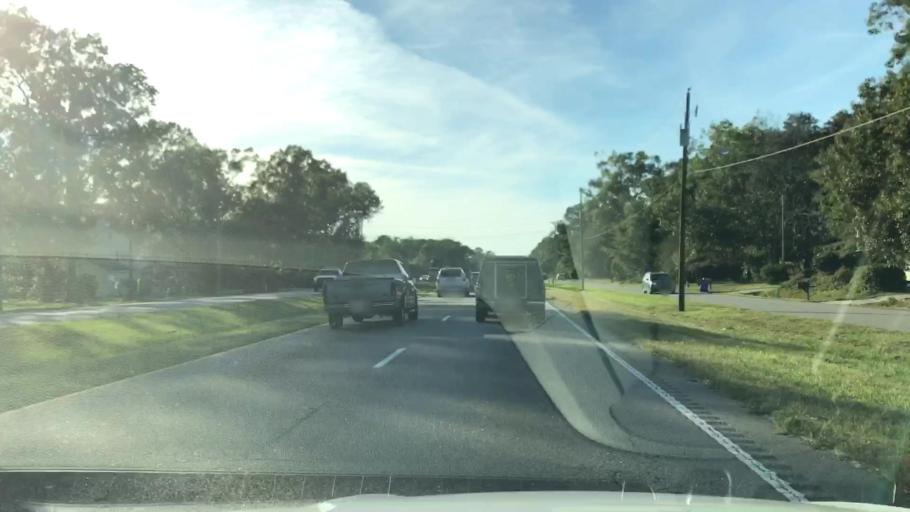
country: US
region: South Carolina
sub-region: Charleston County
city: Shell Point
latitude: 32.7958
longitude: -80.0736
